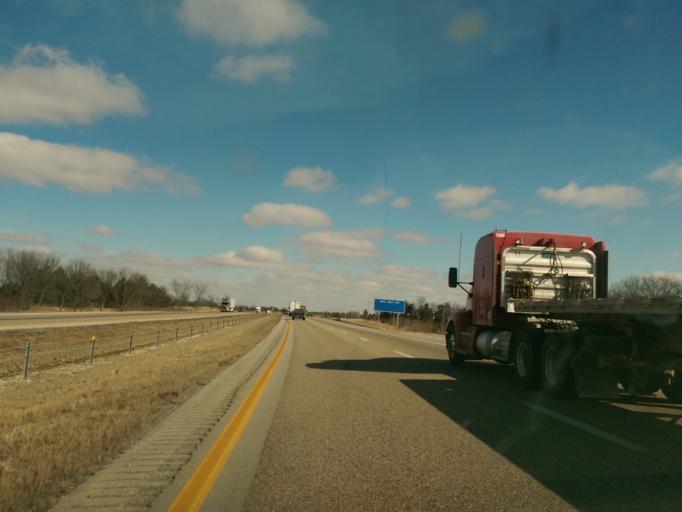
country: US
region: Missouri
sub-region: Montgomery County
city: Montgomery City
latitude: 38.9037
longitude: -91.5529
